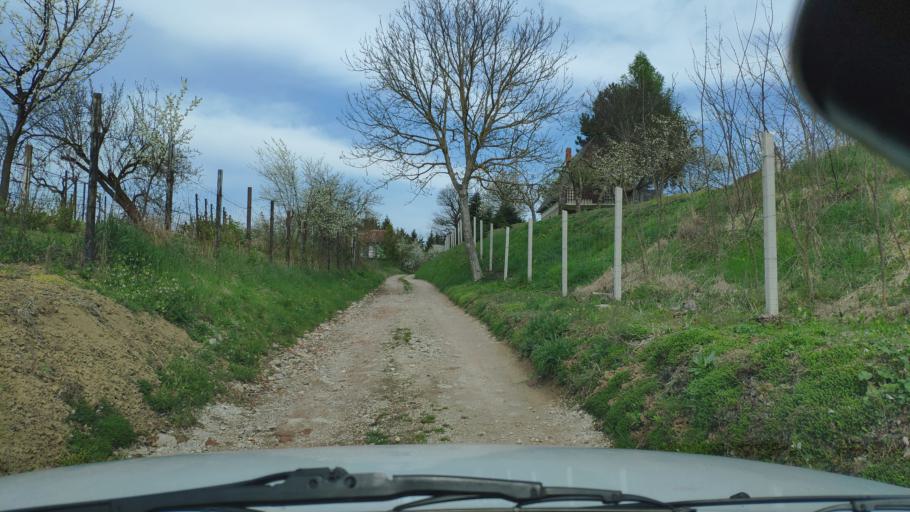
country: HU
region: Zala
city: Nagykanizsa
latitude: 46.4254
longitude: 17.0159
